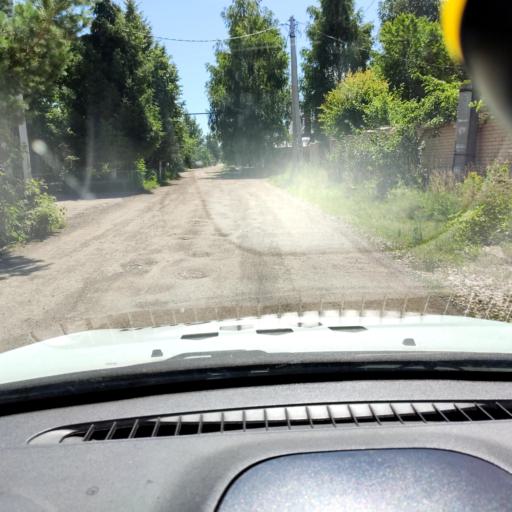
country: RU
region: Samara
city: Tol'yatti
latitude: 53.5666
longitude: 49.3863
